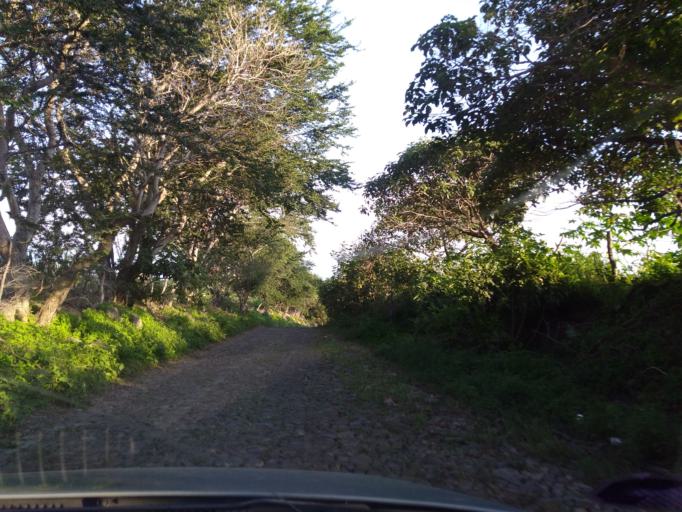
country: MX
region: Jalisco
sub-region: Tonila
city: San Marcos
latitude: 19.4588
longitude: -103.5201
